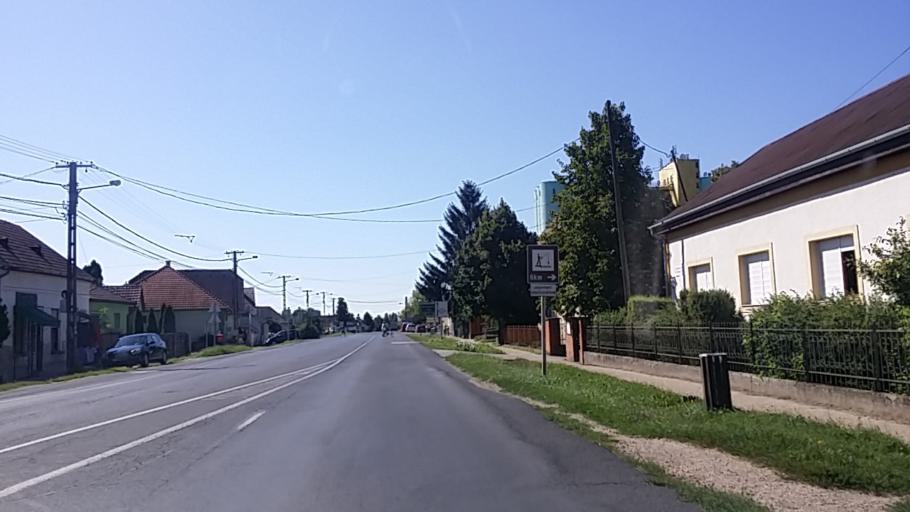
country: HU
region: Fejer
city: Sarbogard
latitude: 46.8578
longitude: 18.6313
